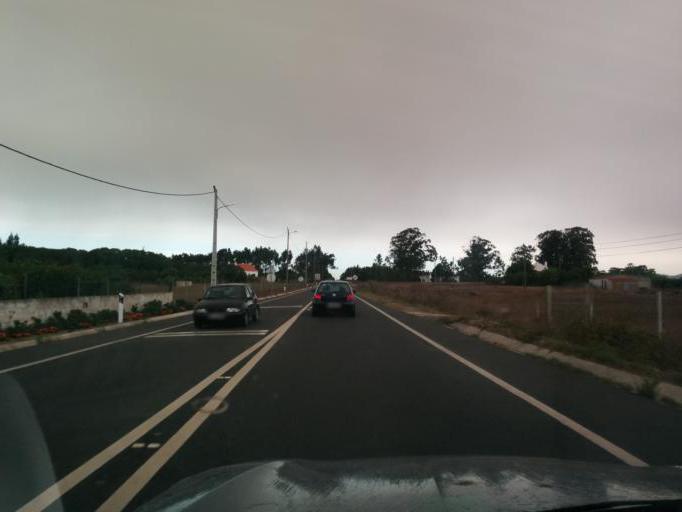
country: PT
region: Beja
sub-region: Odemira
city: Vila Nova de Milfontes
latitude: 37.6566
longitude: -8.7595
